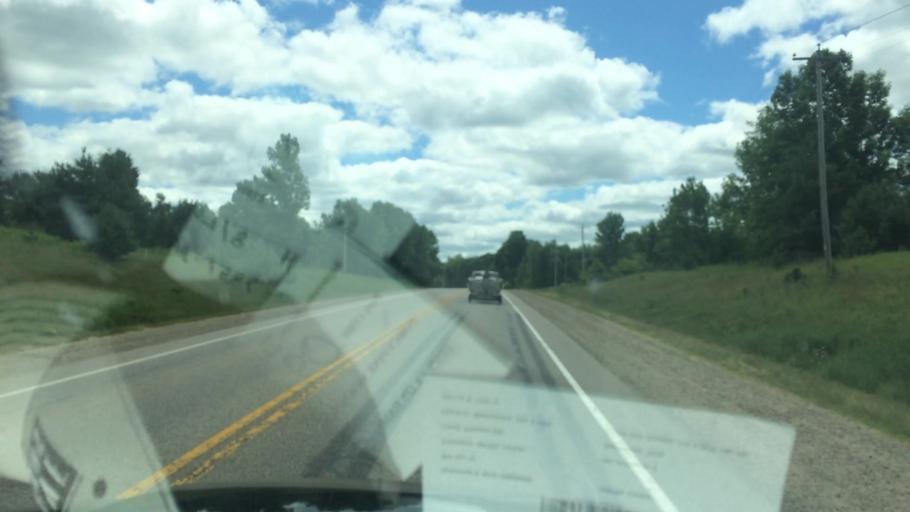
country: US
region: Wisconsin
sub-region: Vilas County
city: Eagle River
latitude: 45.7954
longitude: -89.3206
